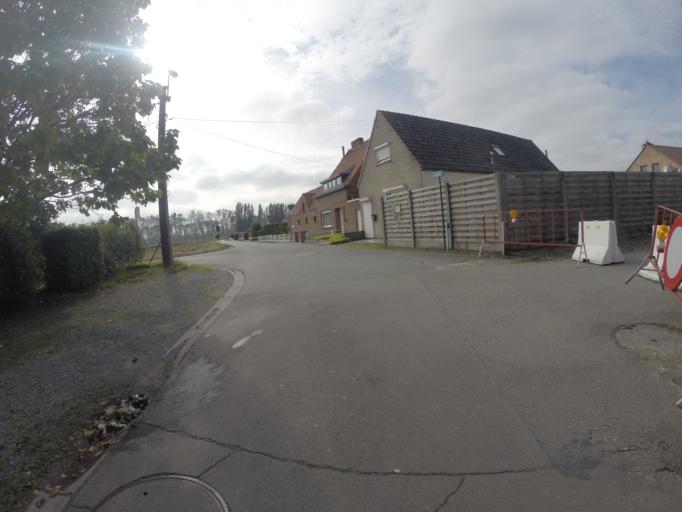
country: BE
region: Flanders
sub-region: Provincie Oost-Vlaanderen
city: Aalter
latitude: 51.0709
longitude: 3.4338
